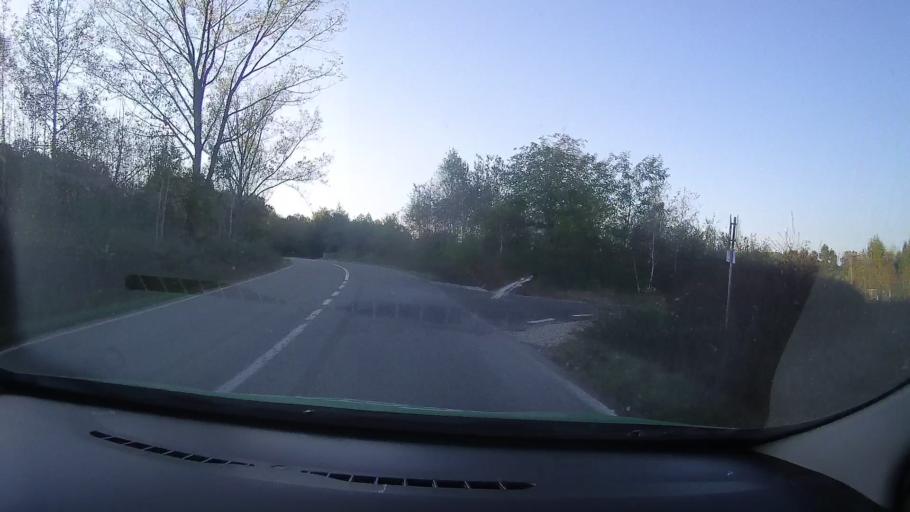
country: RO
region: Timis
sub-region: Comuna Fardea
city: Fardea
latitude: 45.7462
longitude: 22.1401
